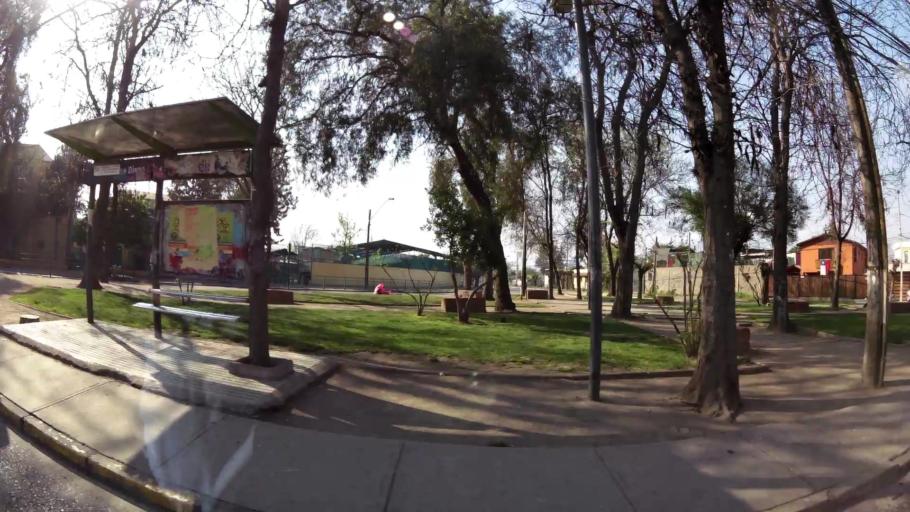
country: CL
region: Santiago Metropolitan
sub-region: Provincia de Santiago
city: Lo Prado
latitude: -33.3842
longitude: -70.6774
